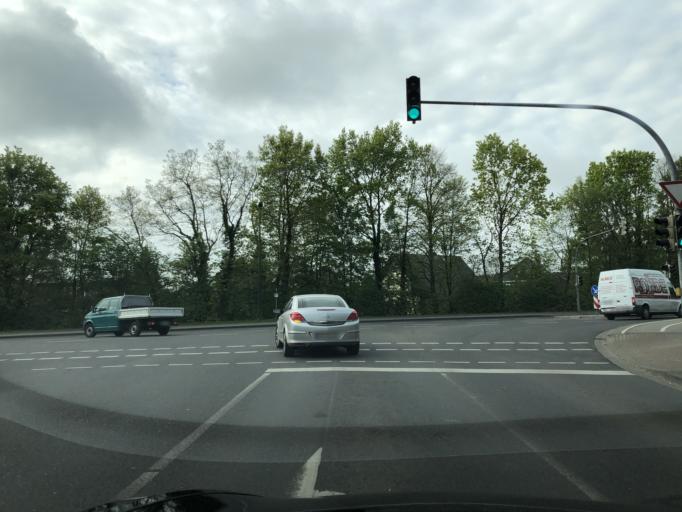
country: DE
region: Mecklenburg-Vorpommern
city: Lubz
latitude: 53.4660
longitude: 12.0292
